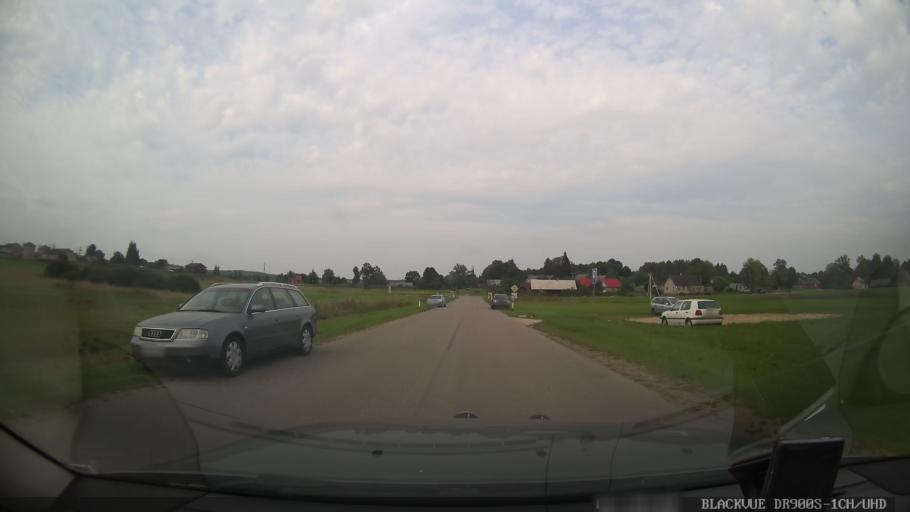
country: LT
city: Skaidiskes
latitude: 54.5405
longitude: 25.6489
